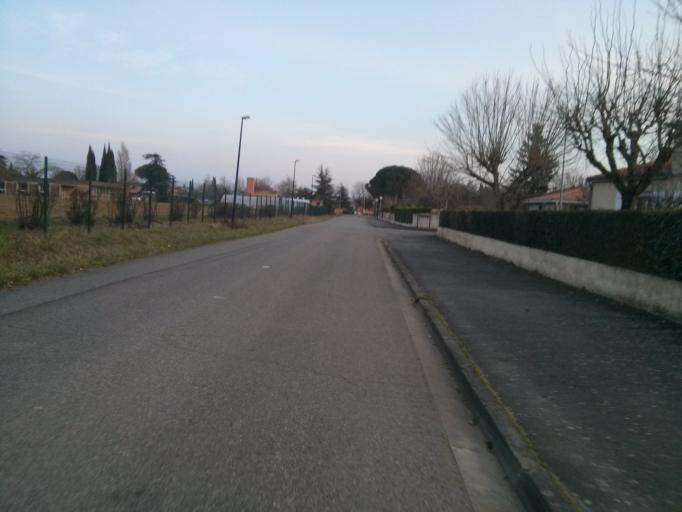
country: FR
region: Midi-Pyrenees
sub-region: Departement de la Haute-Garonne
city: Castanet-Tolosan
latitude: 43.5293
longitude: 1.4976
